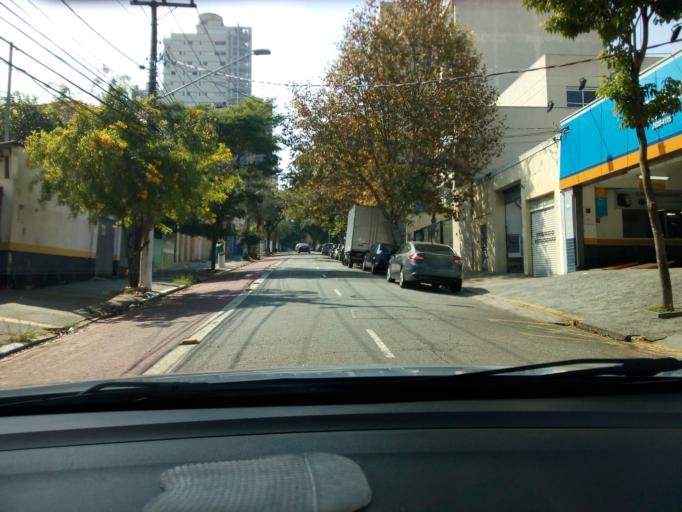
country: BR
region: Sao Paulo
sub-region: Sao Paulo
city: Sao Paulo
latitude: -23.5894
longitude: -46.6471
